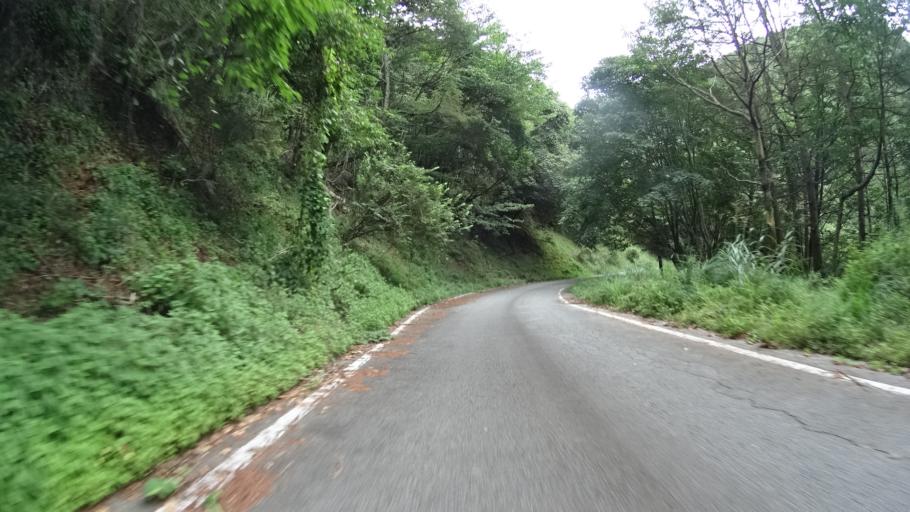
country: JP
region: Yamanashi
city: Nirasaki
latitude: 35.8098
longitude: 138.5480
